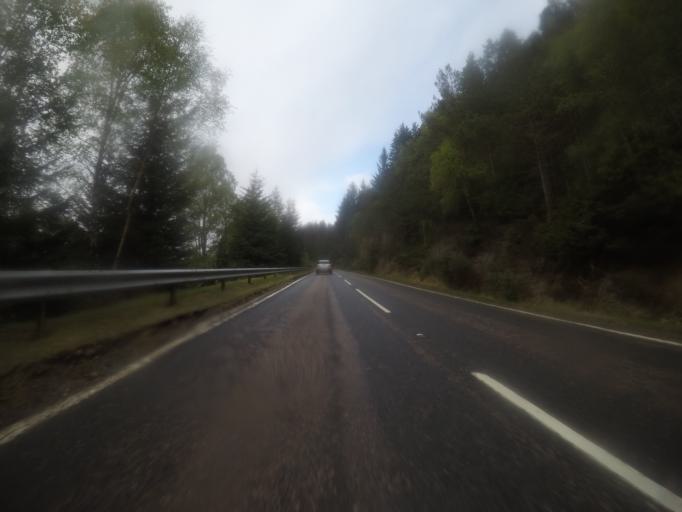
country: GB
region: Scotland
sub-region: Highland
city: Spean Bridge
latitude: 57.0831
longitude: -4.9313
